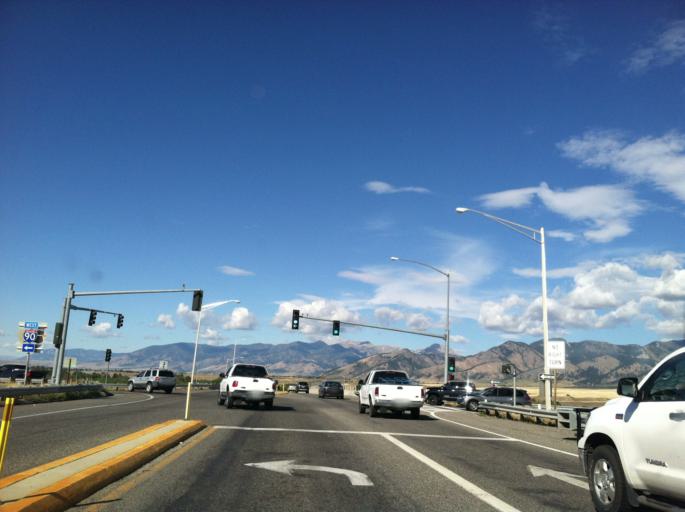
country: US
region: Montana
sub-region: Gallatin County
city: Bozeman
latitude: 45.7159
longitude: -111.0638
